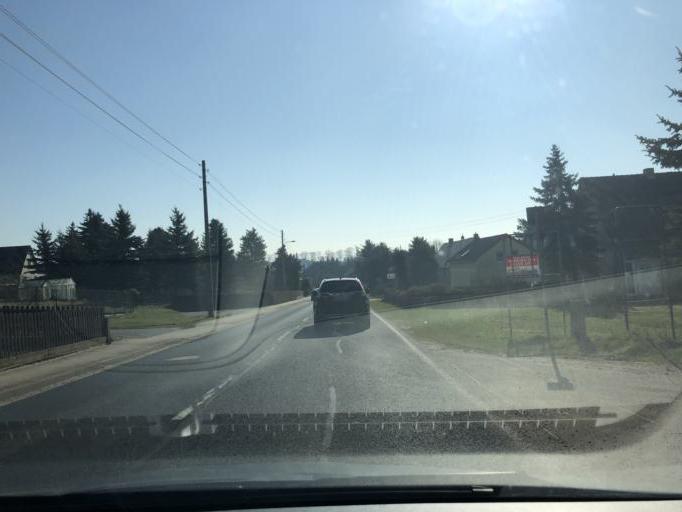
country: DE
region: Saxony
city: Bischofswerda
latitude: 51.1428
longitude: 14.1734
